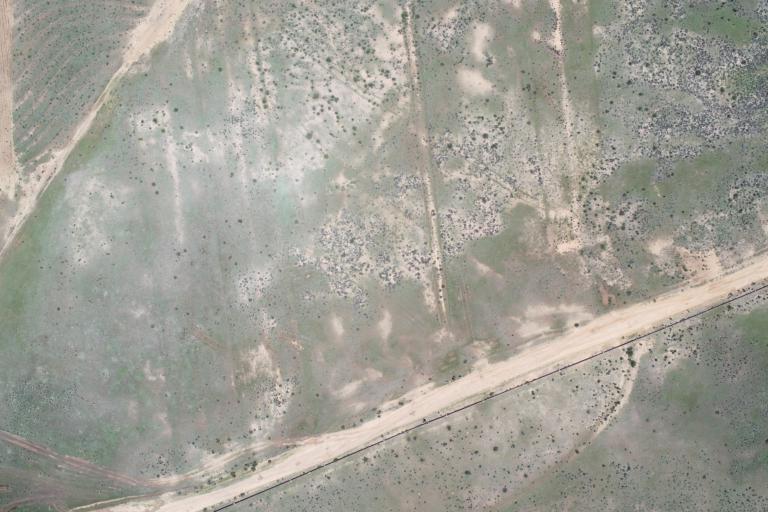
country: BO
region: La Paz
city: Patacamaya
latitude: -17.2753
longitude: -68.5083
